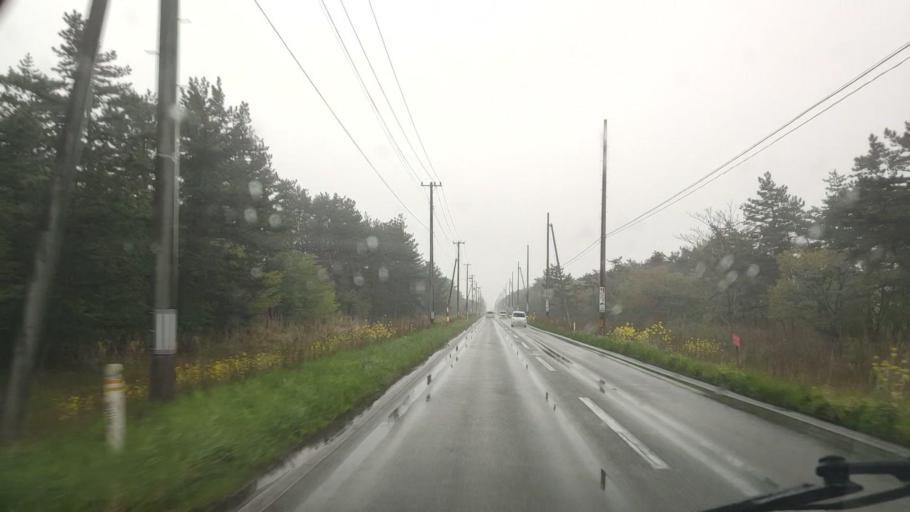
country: JP
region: Akita
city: Tenno
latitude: 40.0092
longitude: 139.9512
